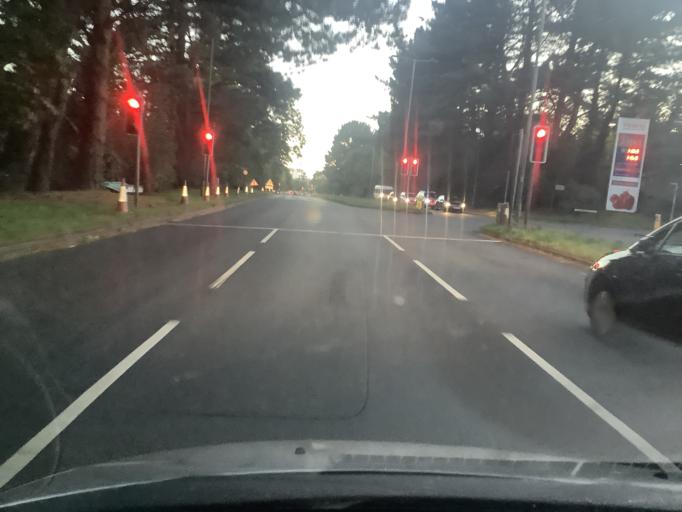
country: GB
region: England
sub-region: Hampshire
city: Marchwood
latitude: 50.9239
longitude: -1.4449
